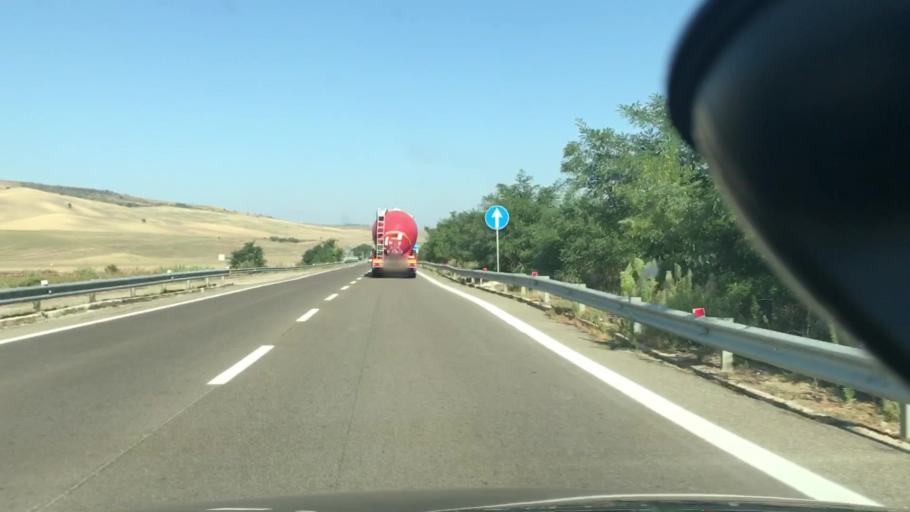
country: IT
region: Basilicate
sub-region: Provincia di Matera
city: Irsina
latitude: 40.7907
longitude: 16.2841
